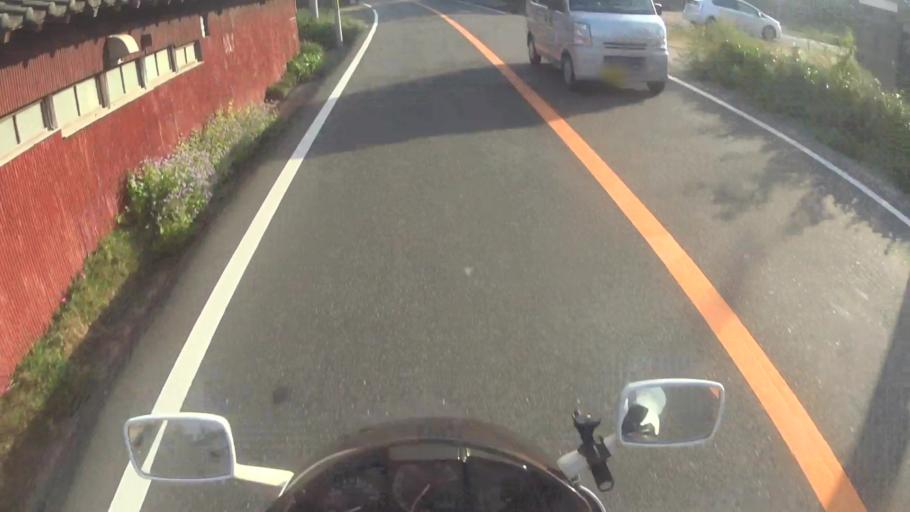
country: JP
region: Kyoto
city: Miyazu
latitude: 35.6563
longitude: 135.0925
